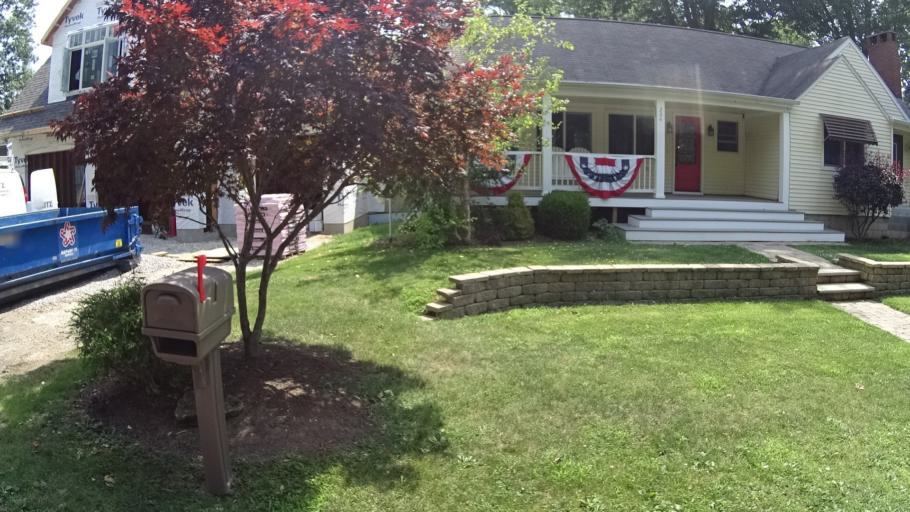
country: US
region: Ohio
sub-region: Erie County
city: Huron
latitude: 41.4093
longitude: -82.5830
